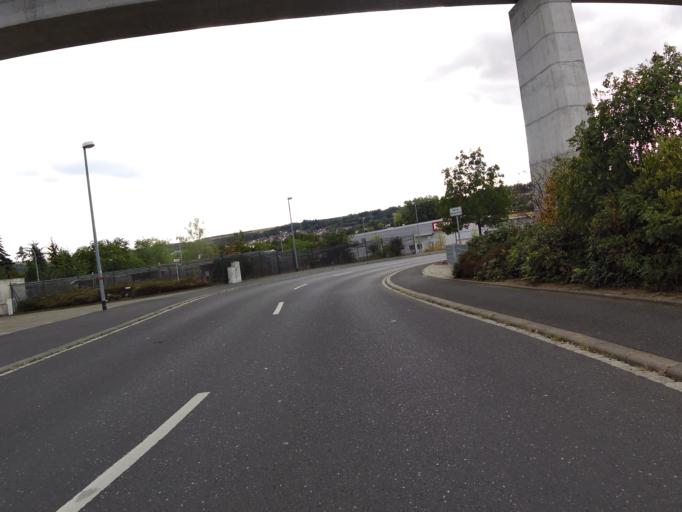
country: DE
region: Bavaria
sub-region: Regierungsbezirk Unterfranken
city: Veitshochheim
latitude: 49.8239
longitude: 9.8756
